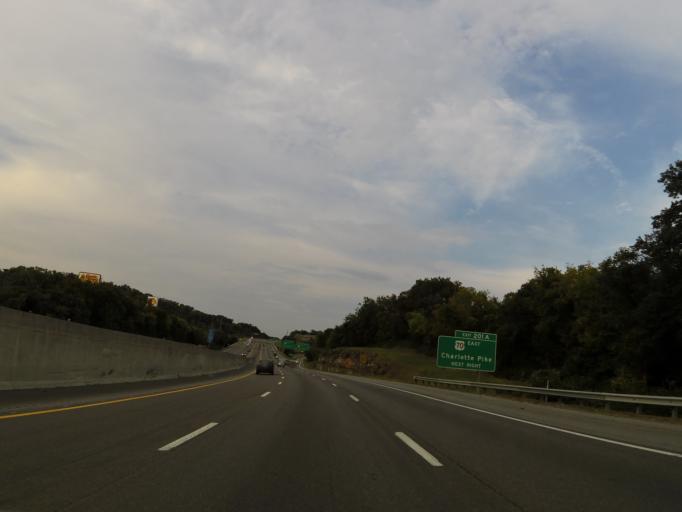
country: US
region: Tennessee
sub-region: Davidson County
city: Belle Meade
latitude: 36.1273
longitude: -86.9020
